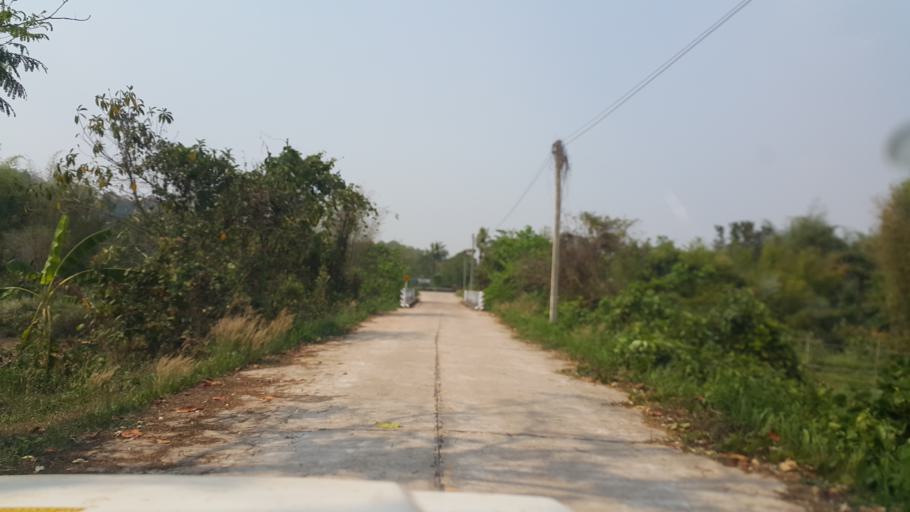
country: TH
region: Nakhon Phanom
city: Ban Phaeng
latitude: 17.9852
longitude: 104.1453
